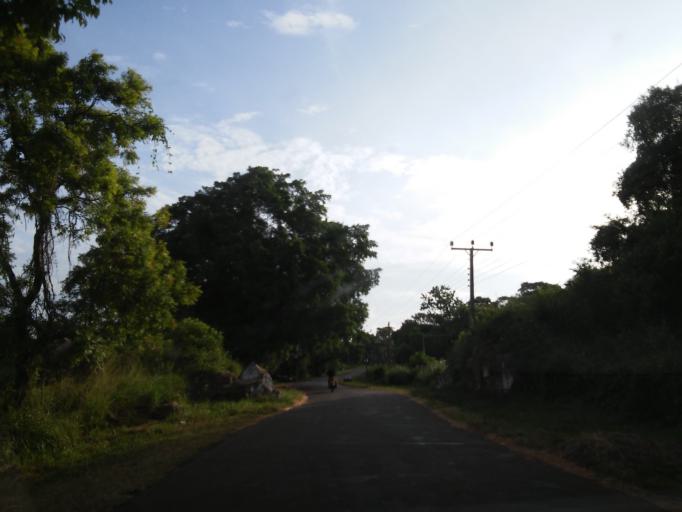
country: LK
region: Central
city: Sigiriya
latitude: 8.1525
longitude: 80.6480
